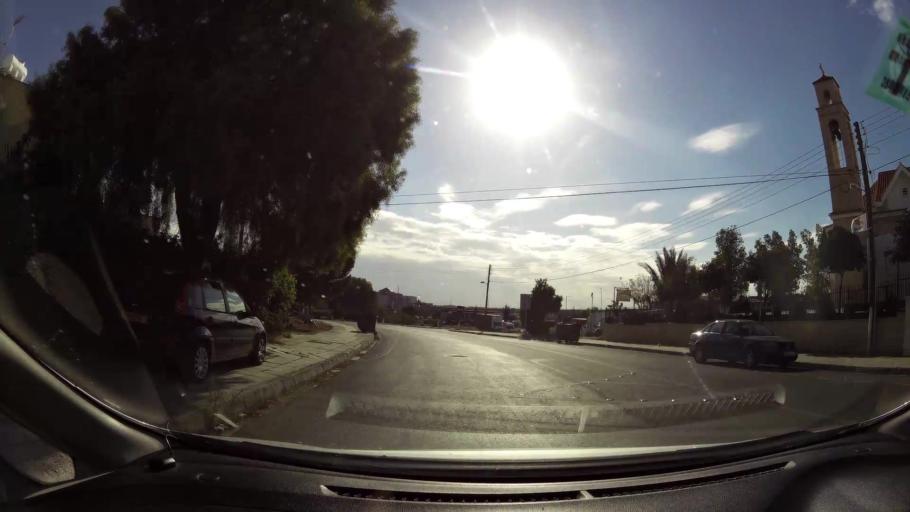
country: CY
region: Lefkosia
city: Nicosia
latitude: 35.1300
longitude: 33.3622
